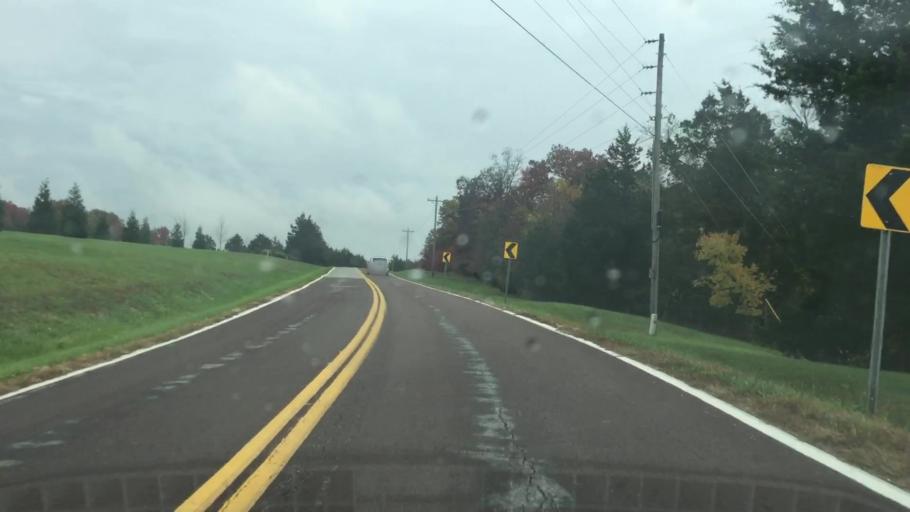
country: US
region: Missouri
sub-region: Callaway County
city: Fulton
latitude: 38.7786
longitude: -91.8439
